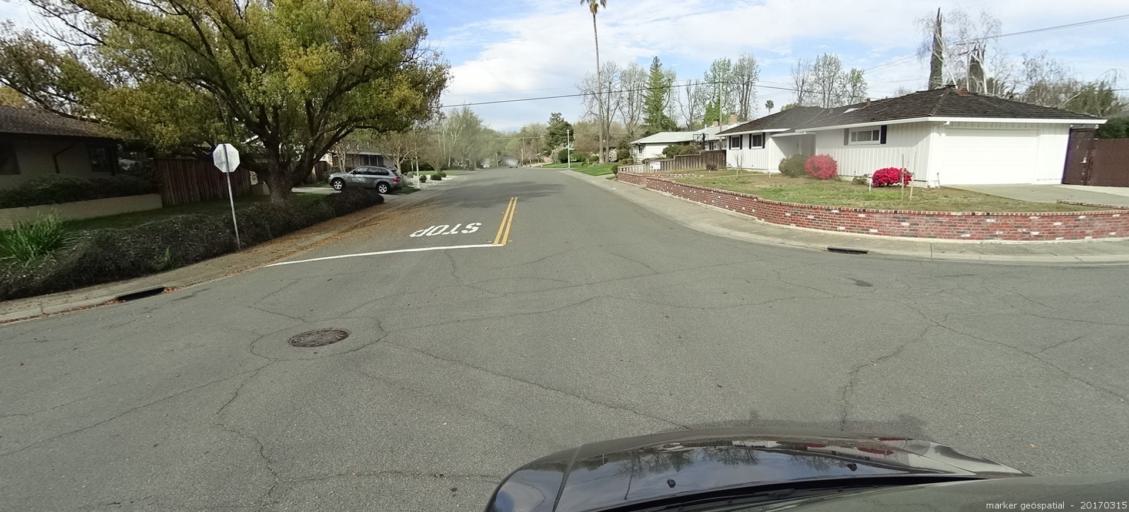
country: US
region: California
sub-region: Sacramento County
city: Parkway
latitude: 38.5105
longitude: -121.5126
